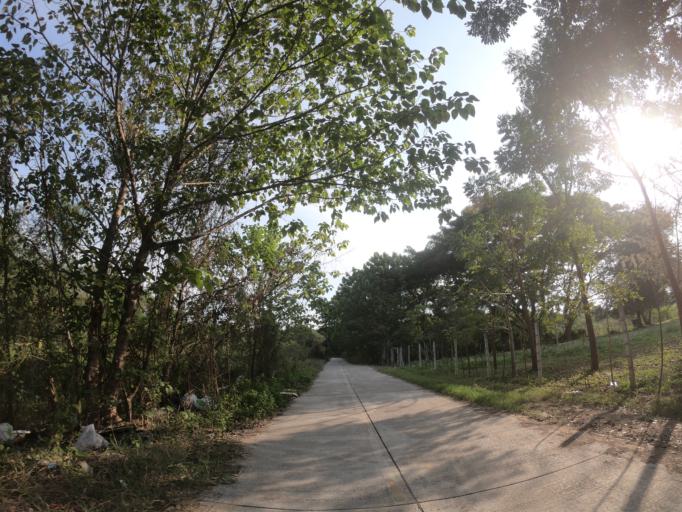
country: TH
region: Chiang Mai
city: Saraphi
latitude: 18.7341
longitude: 98.9828
